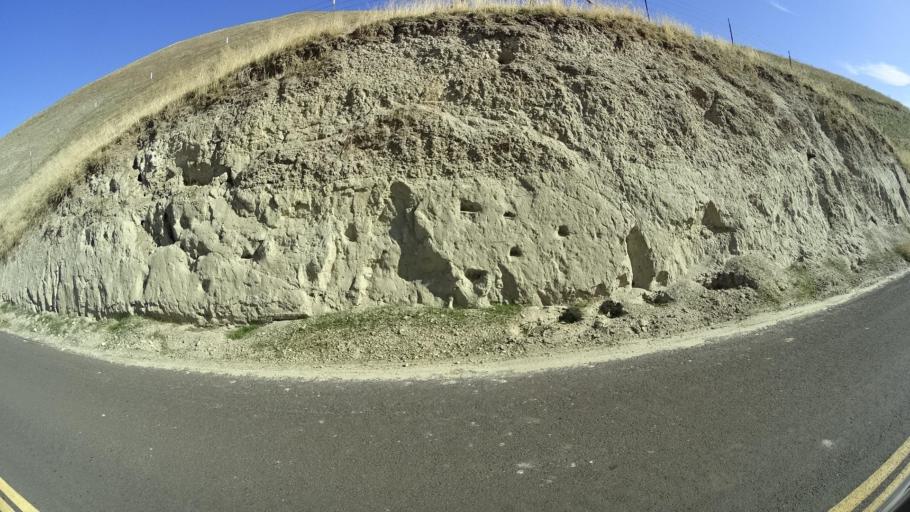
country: US
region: California
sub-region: Tulare County
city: Richgrove
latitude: 35.6665
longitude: -118.9152
